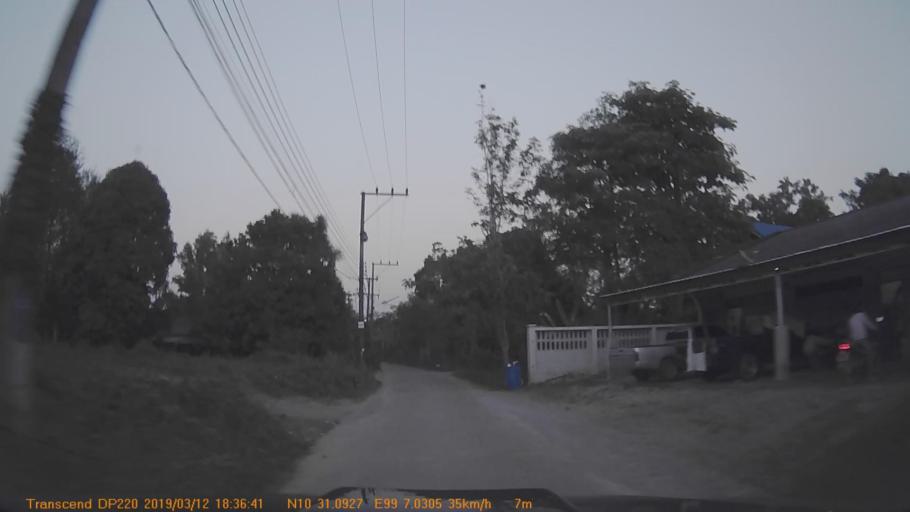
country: TH
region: Chumphon
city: Chumphon
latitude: 10.5182
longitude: 99.1173
